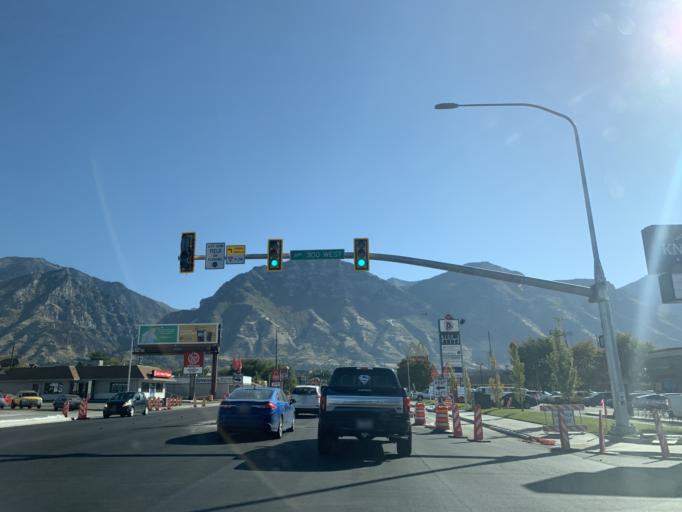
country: US
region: Utah
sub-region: Utah County
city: Provo
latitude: 40.2505
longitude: -111.6640
